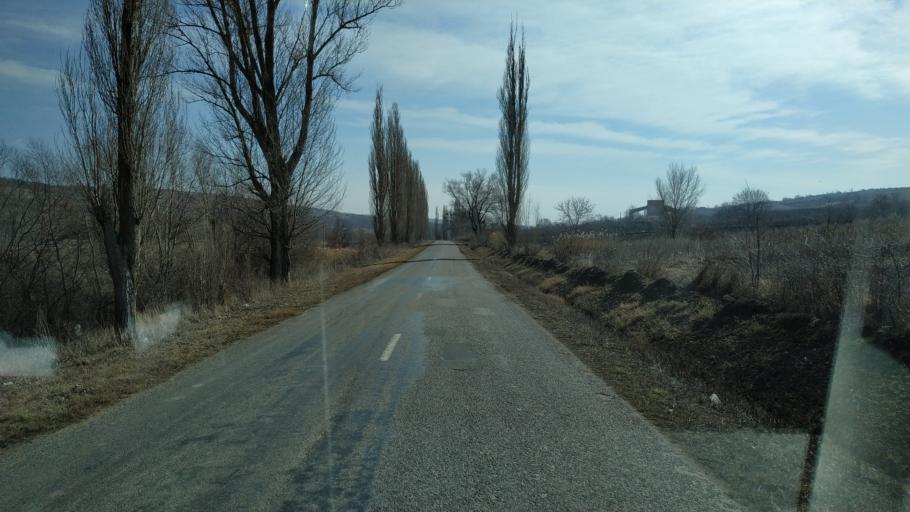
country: MD
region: Nisporeni
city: Nisporeni
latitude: 47.1644
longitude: 28.1007
